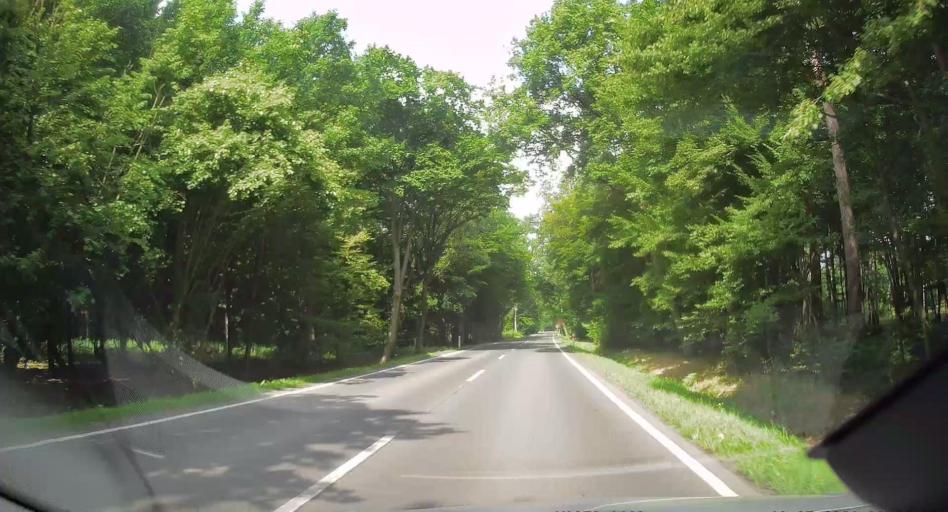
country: PL
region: Opole Voivodeship
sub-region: Powiat prudnicki
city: Twardawa
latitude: 50.3389
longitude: 18.0362
